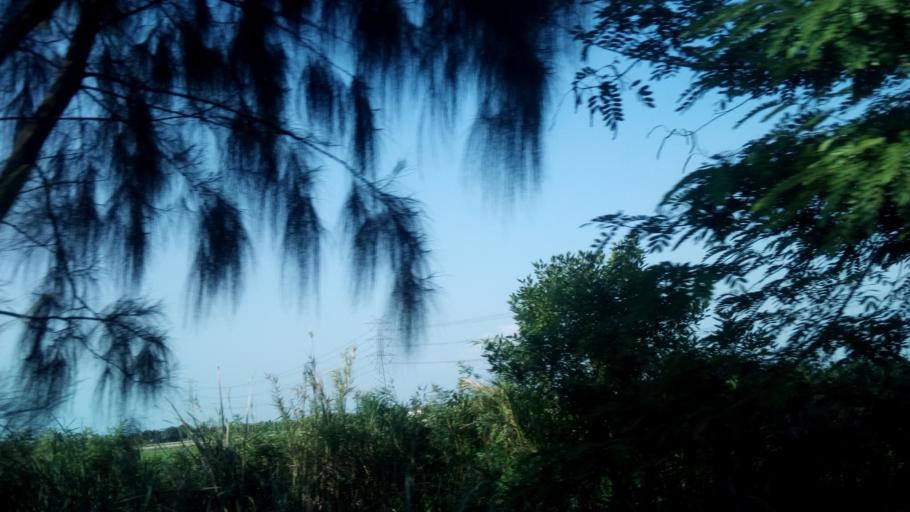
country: TH
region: Nonthaburi
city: Sai Noi
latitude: 13.9371
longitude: 100.3394
